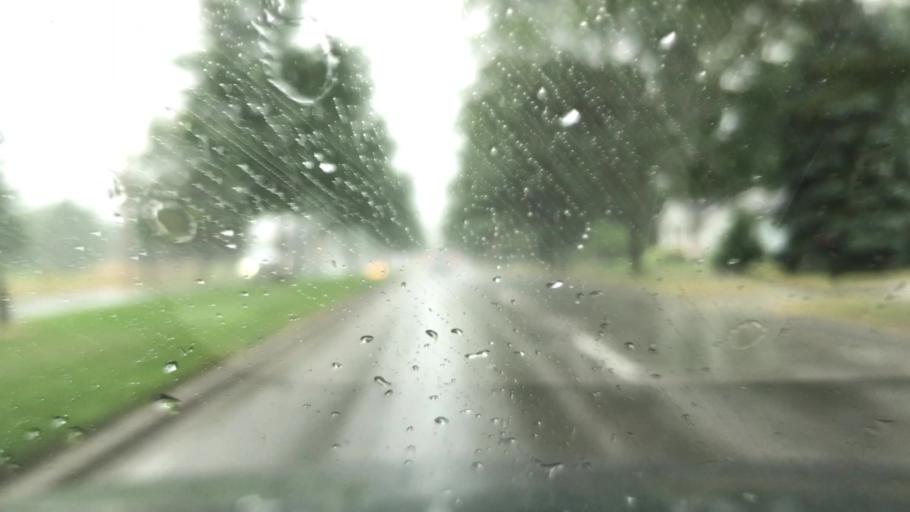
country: US
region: Michigan
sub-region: Kent County
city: Wyoming
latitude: 42.8763
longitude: -85.7238
